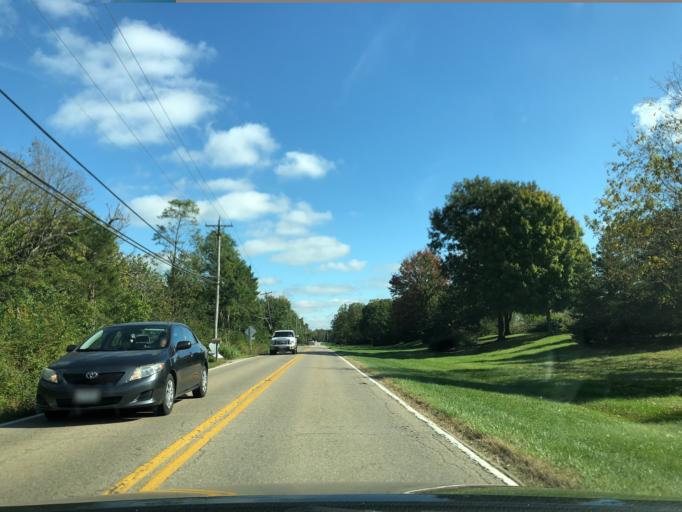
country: US
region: Ohio
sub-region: Hamilton County
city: The Village of Indian Hill
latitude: 39.2417
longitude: -84.2788
